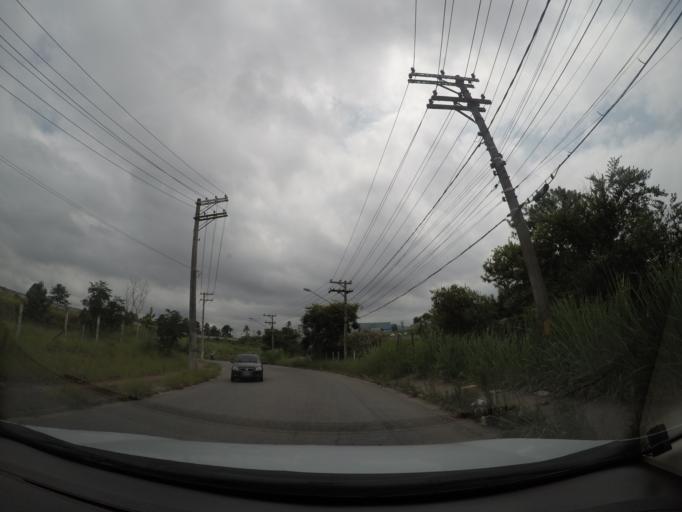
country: BR
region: Sao Paulo
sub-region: Itaquaquecetuba
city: Itaquaquecetuba
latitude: -23.4516
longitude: -46.3825
